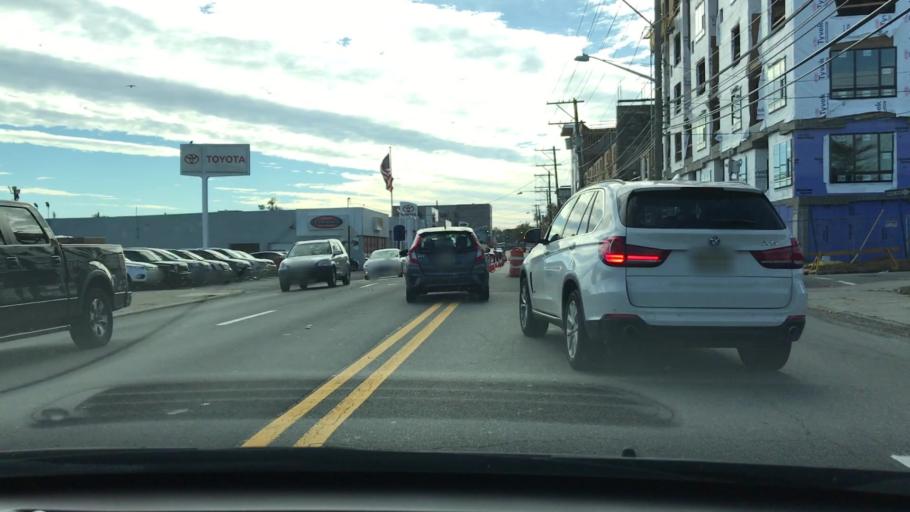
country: US
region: New Jersey
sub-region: Bergen County
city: Hackensack
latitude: 40.8880
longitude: -74.0390
